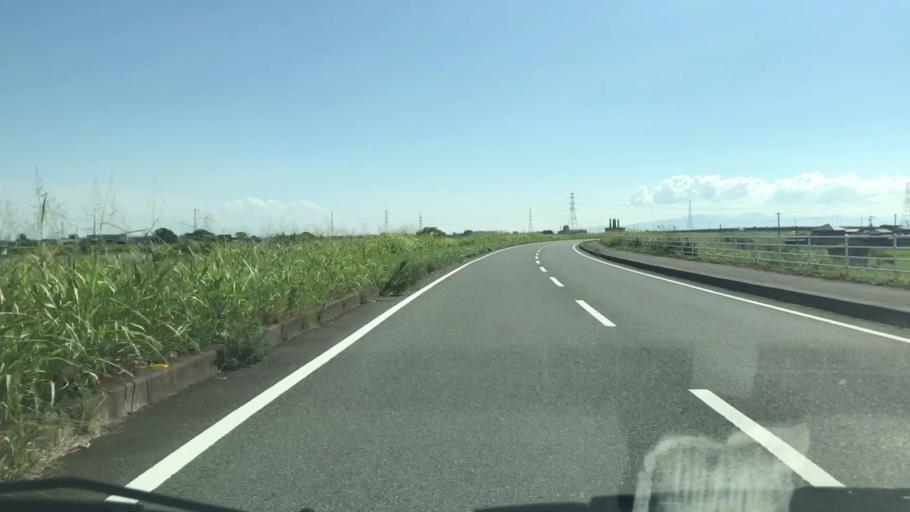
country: JP
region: Saga Prefecture
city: Kanzakimachi-kanzaki
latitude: 33.2552
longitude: 130.4137
